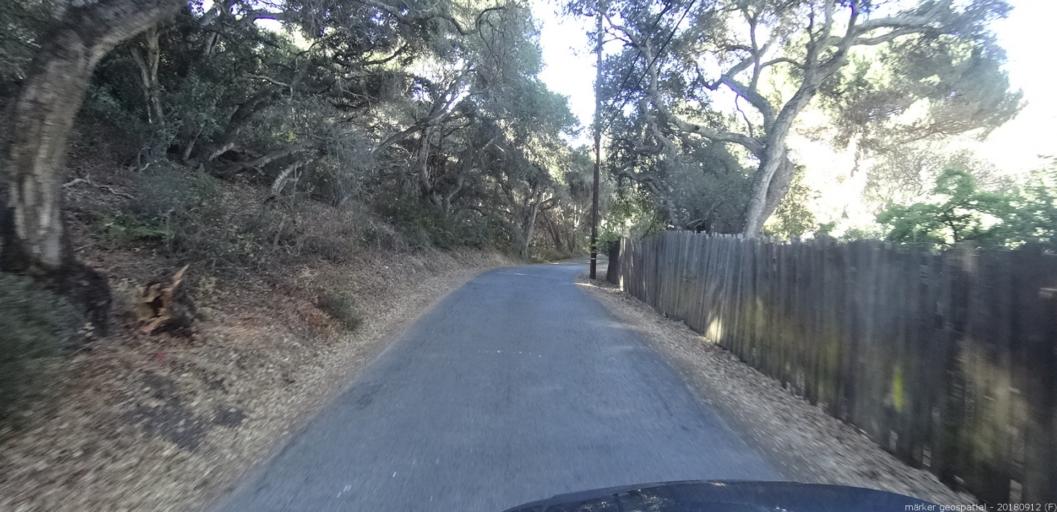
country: US
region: California
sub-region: Monterey County
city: Carmel Valley Village
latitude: 36.5448
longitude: -121.7348
